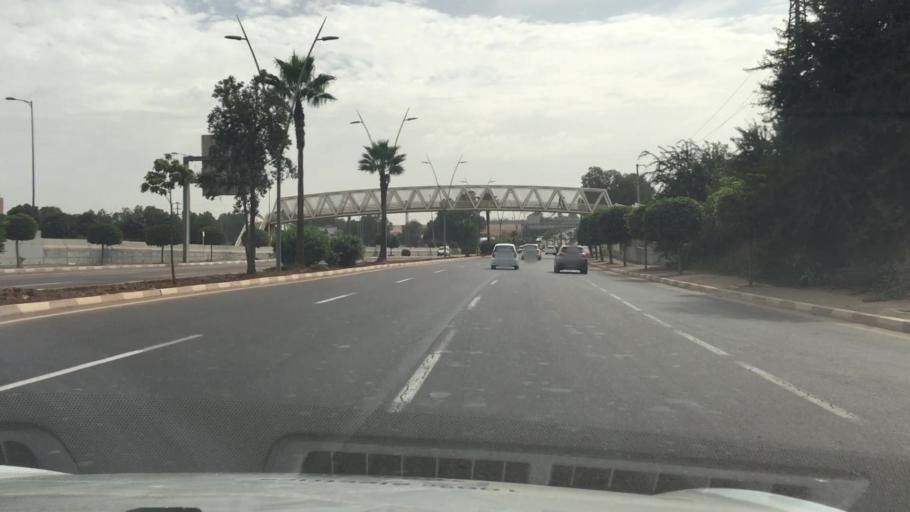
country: MA
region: Grand Casablanca
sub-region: Nouaceur
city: Bouskoura
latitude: 33.5160
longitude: -7.6318
